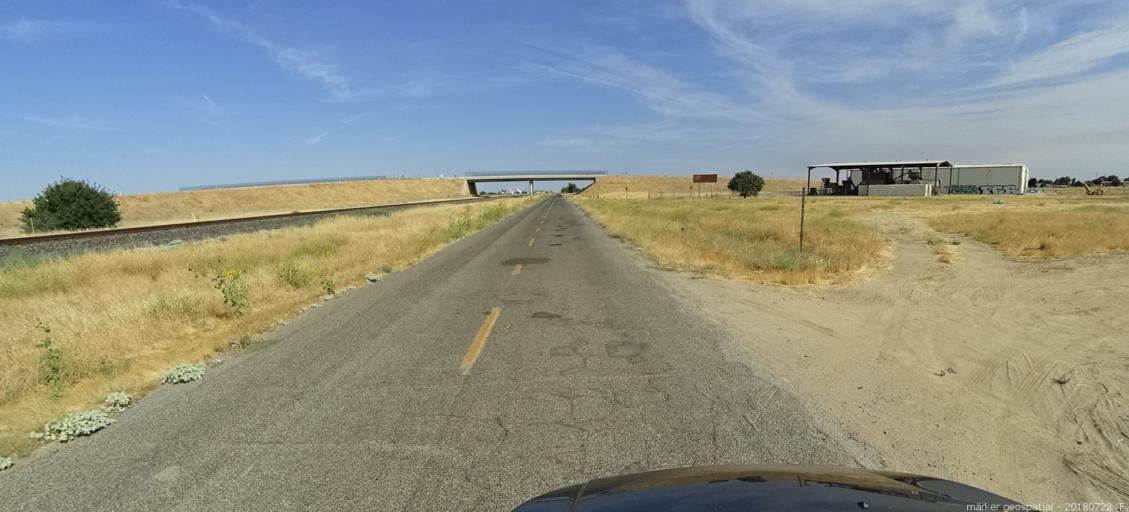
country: US
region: California
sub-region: Madera County
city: Fairmead
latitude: 37.0646
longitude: -120.1832
